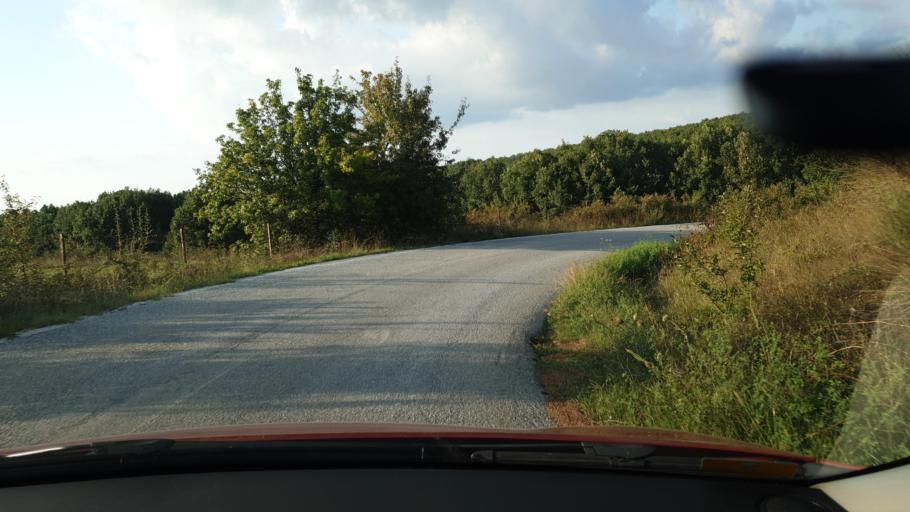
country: GR
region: Central Macedonia
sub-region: Nomos Chalkidikis
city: Galatista
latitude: 40.5324
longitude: 23.2766
